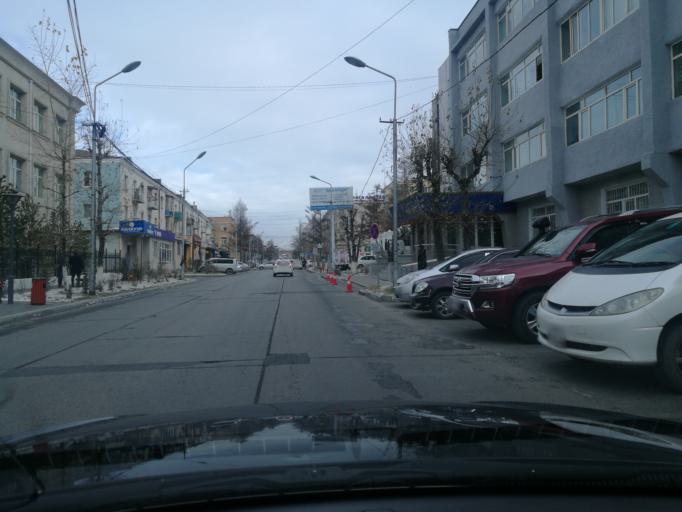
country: MN
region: Ulaanbaatar
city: Ulaanbaatar
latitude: 47.9135
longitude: 106.8988
